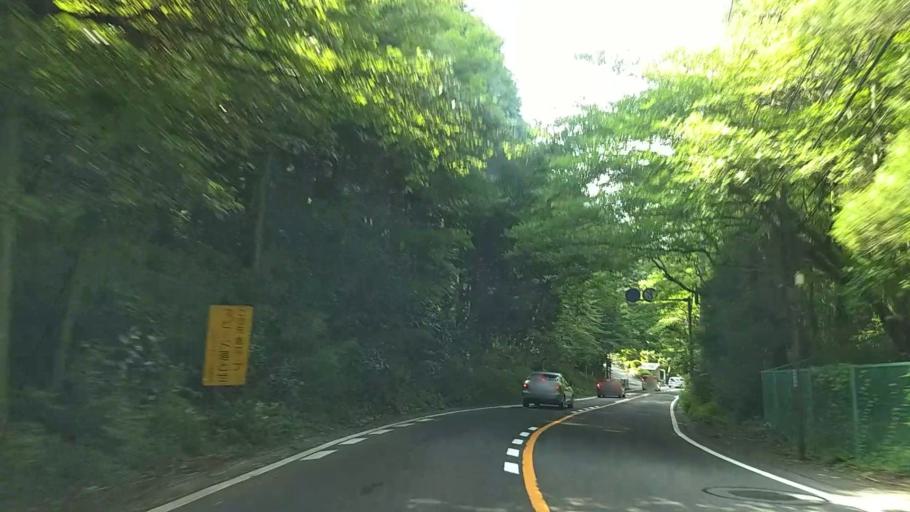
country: JP
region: Kanagawa
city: Hakone
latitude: 35.2282
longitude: 139.0491
